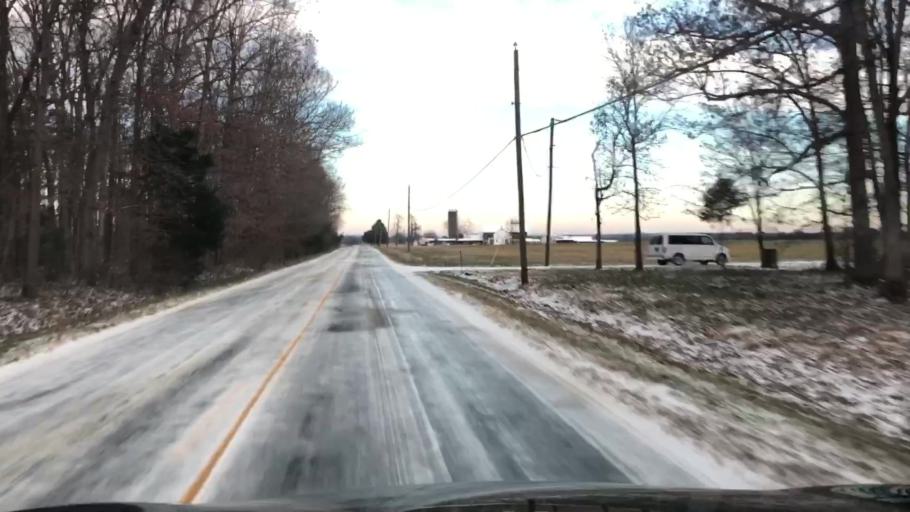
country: US
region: Virginia
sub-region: Prince William County
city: Nokesville
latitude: 38.6402
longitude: -77.6751
